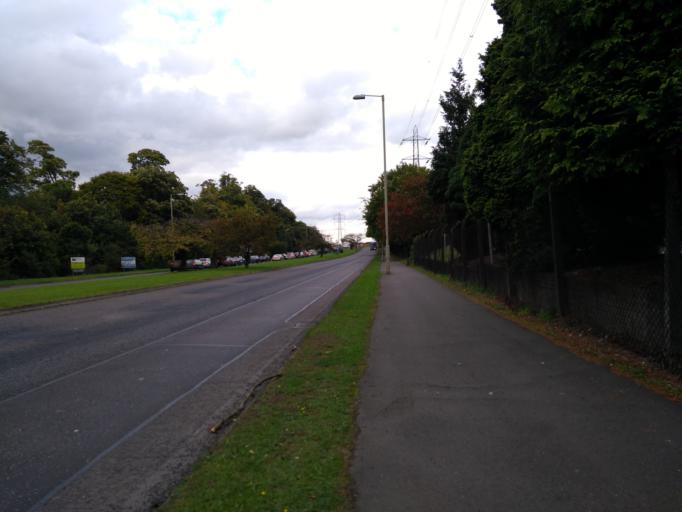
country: GB
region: England
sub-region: Central Bedfordshire
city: Houghton Regis
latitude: 51.8984
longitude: -0.5084
